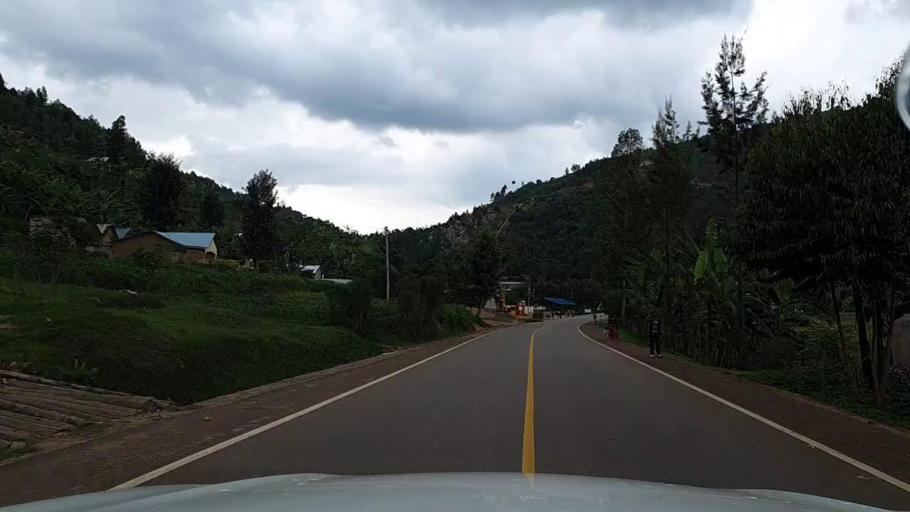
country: RW
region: Northern Province
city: Byumba
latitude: -1.6751
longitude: 30.0929
